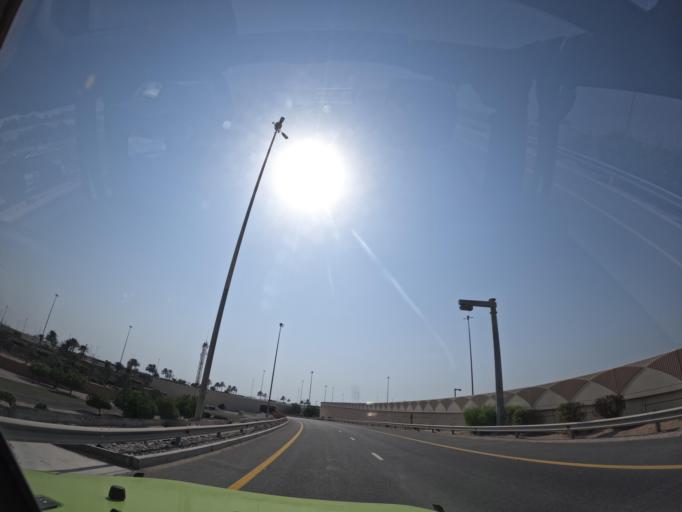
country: AE
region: Abu Dhabi
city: Abu Dhabi
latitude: 24.4870
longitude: 54.6439
